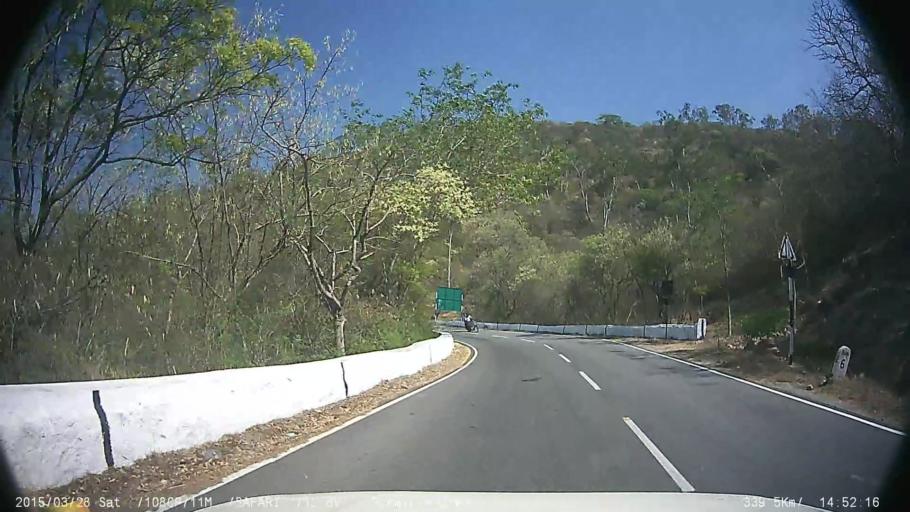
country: IN
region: Karnataka
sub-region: Mysore
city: Mysore
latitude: 12.2851
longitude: 76.6883
